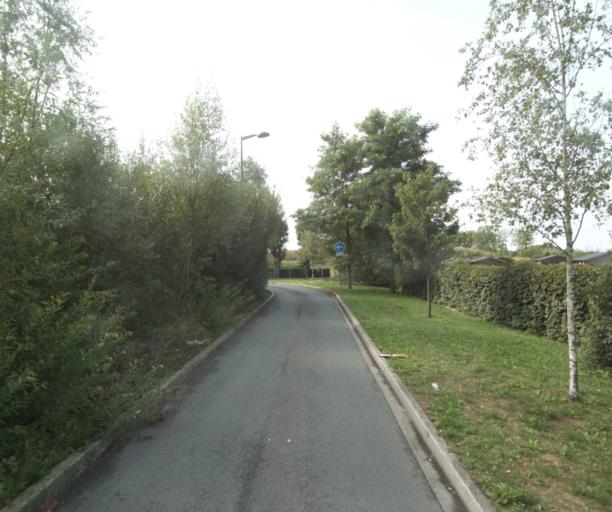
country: FR
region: Nord-Pas-de-Calais
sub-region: Departement du Nord
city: Marquette-lez-Lille
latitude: 50.6816
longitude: 3.0797
